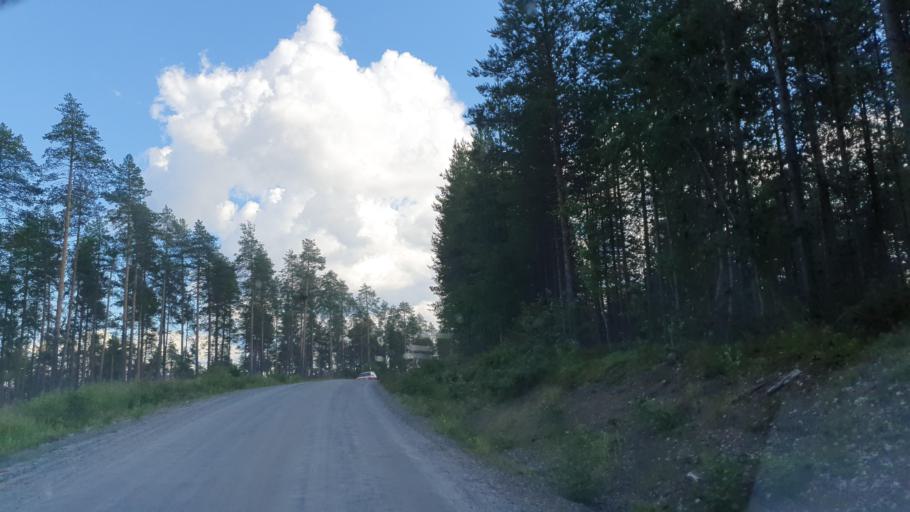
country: FI
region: Kainuu
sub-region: Kehys-Kainuu
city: Kuhmo
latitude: 64.0976
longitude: 29.4100
